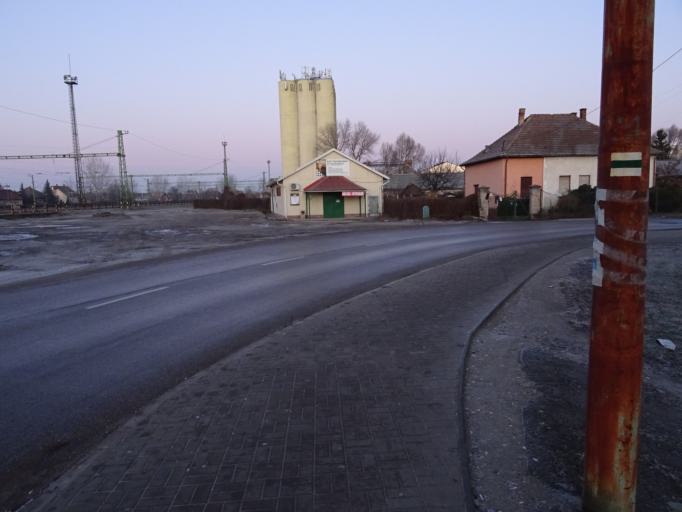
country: HU
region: Pest
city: Nagykata
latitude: 47.4111
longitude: 19.7359
